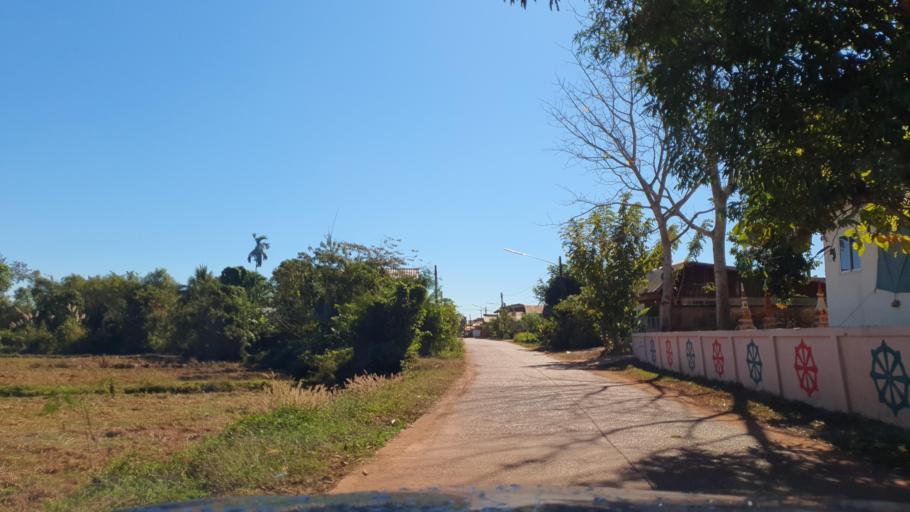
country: TH
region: Nakhon Phanom
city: Ban Phaeng
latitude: 17.8299
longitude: 104.2657
